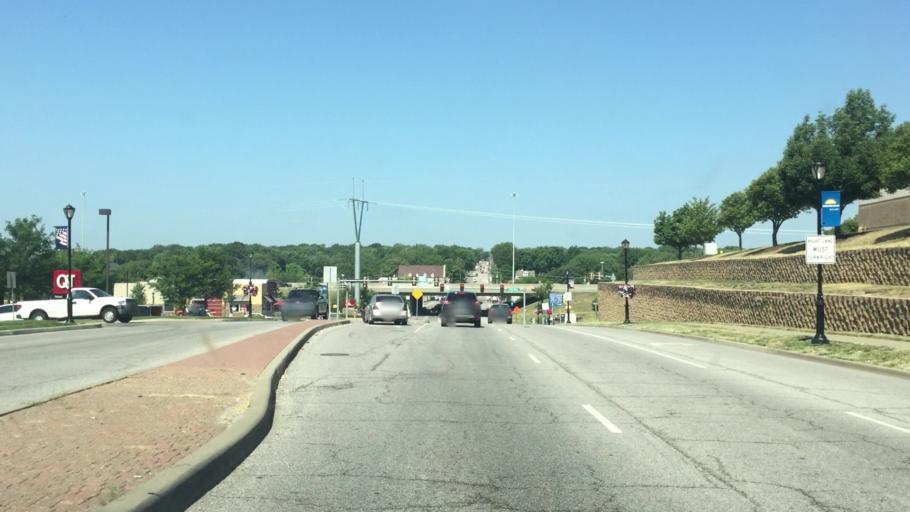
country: US
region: Kansas
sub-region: Johnson County
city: Merriam
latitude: 39.0223
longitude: -94.6889
